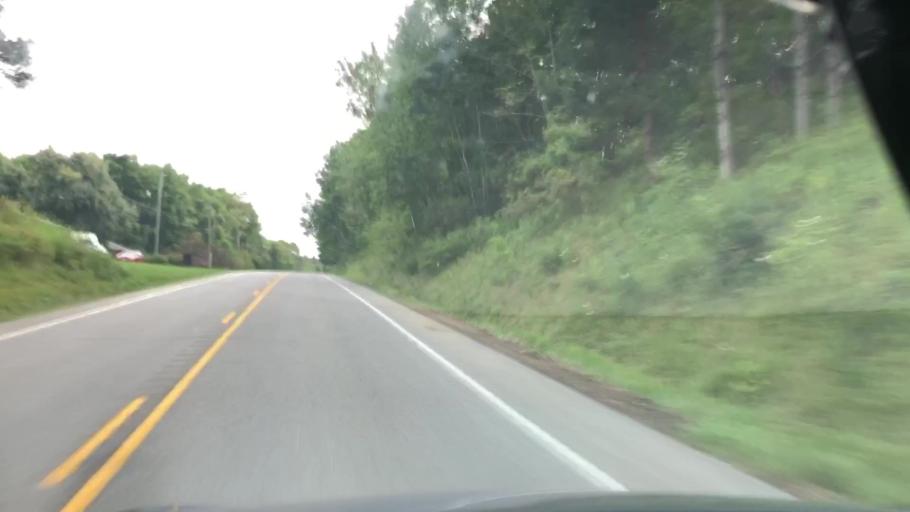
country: US
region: Pennsylvania
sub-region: Crawford County
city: Titusville
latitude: 41.6030
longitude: -79.6770
